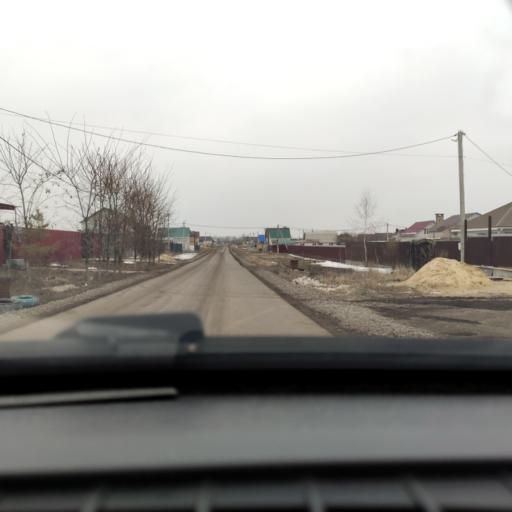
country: RU
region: Voronezj
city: Novaya Usman'
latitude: 51.6593
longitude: 39.4149
